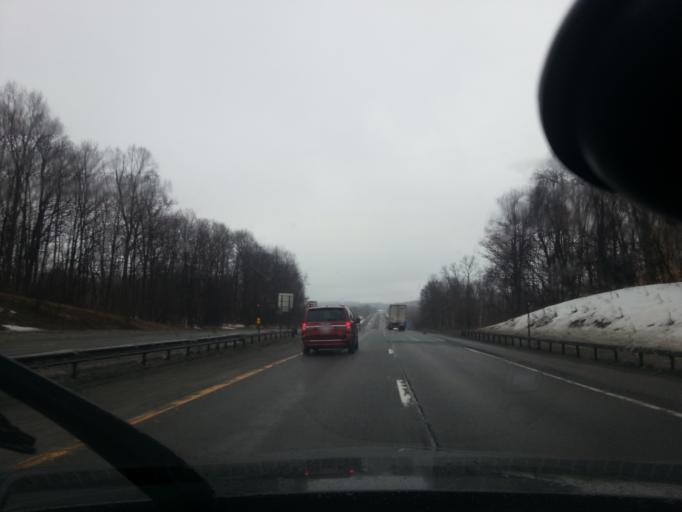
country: US
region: New York
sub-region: Onondaga County
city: Nedrow
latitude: 42.9194
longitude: -76.1211
